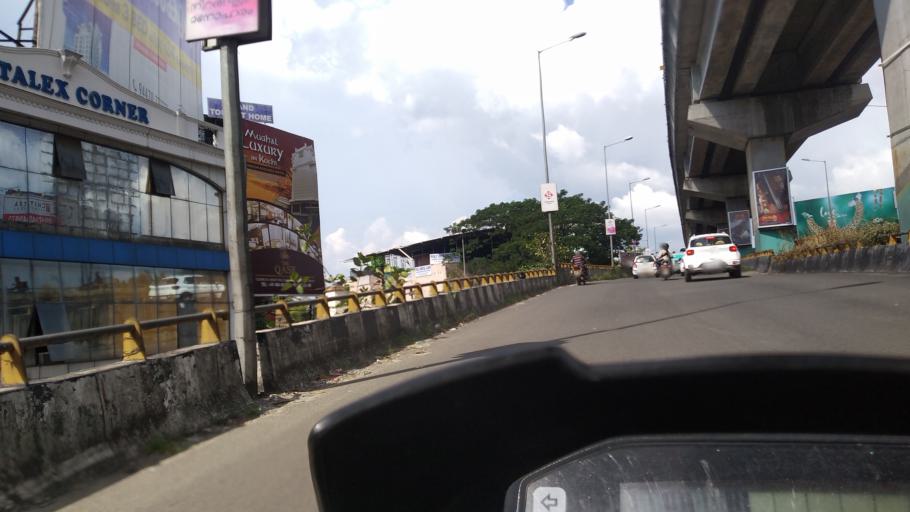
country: IN
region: Kerala
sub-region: Ernakulam
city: Cochin
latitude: 9.9892
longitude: 76.2864
